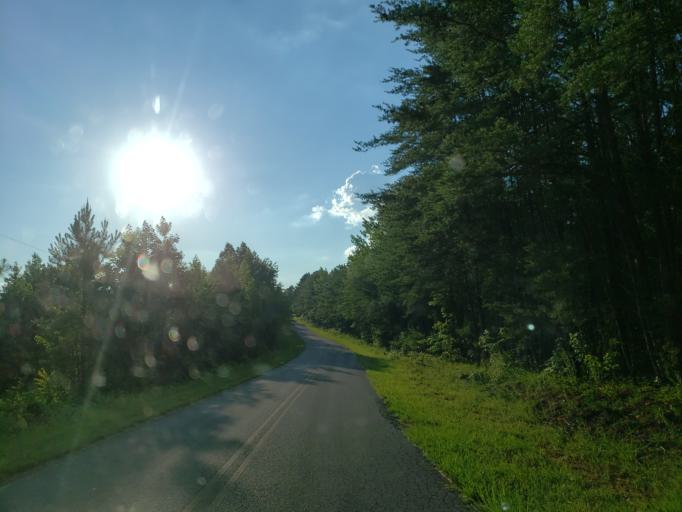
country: US
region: Georgia
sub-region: Haralson County
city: Tallapoosa
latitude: 33.8300
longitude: -85.2794
